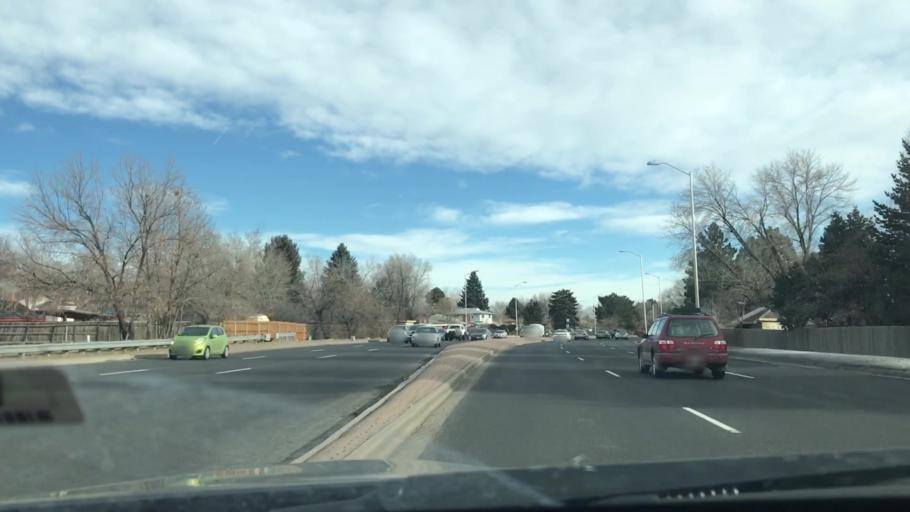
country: US
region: Colorado
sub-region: El Paso County
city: Cimarron Hills
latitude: 38.9005
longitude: -104.7658
